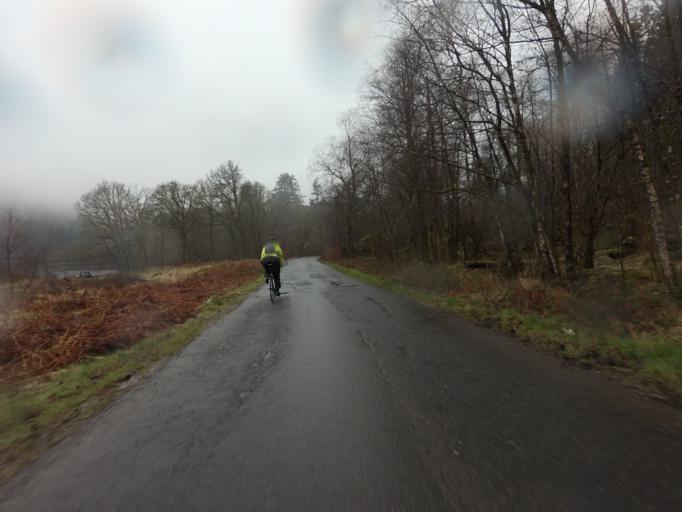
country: GB
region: Scotland
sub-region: West Dunbartonshire
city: Balloch
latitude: 56.2059
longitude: -4.5329
